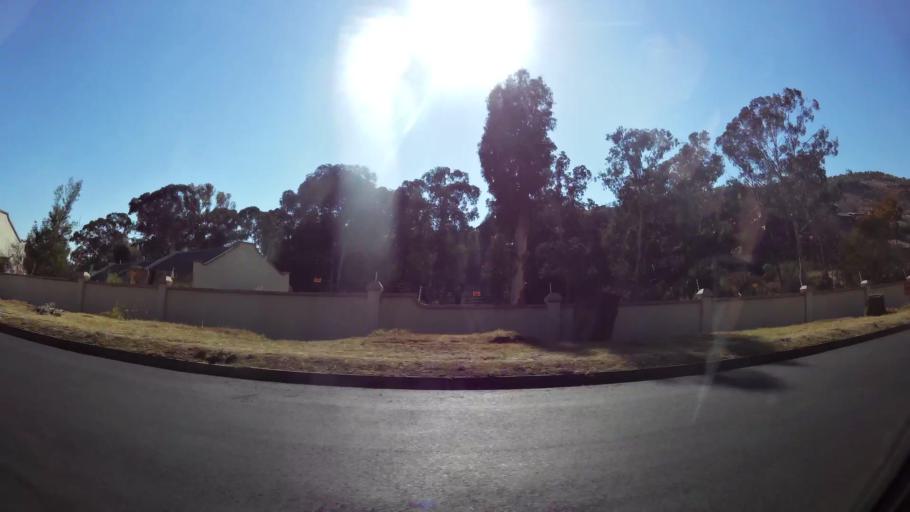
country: ZA
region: Gauteng
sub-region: City of Johannesburg Metropolitan Municipality
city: Roodepoort
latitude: -26.1251
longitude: 27.8776
